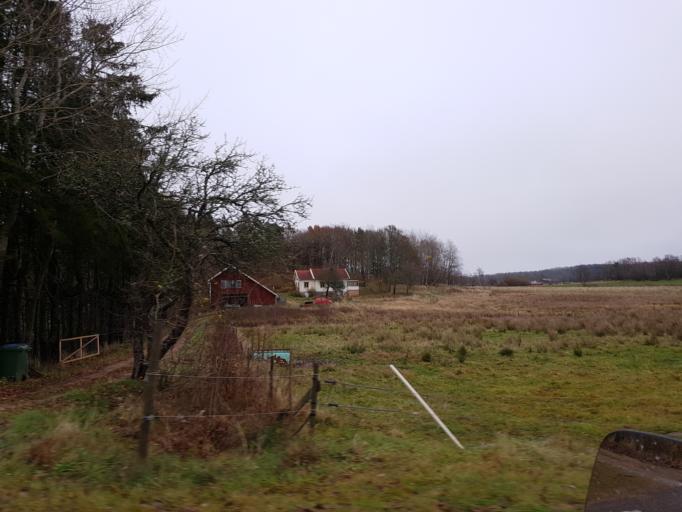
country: SE
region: Vaestra Goetaland
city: Svanesund
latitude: 58.2048
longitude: 11.7757
